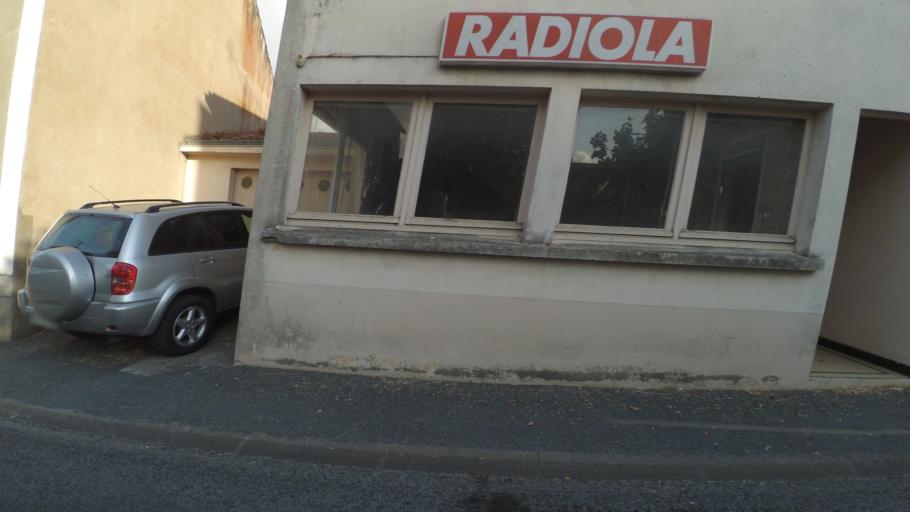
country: FR
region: Pays de la Loire
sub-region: Departement de la Loire-Atlantique
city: La Planche
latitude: 47.0161
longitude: -1.4369
